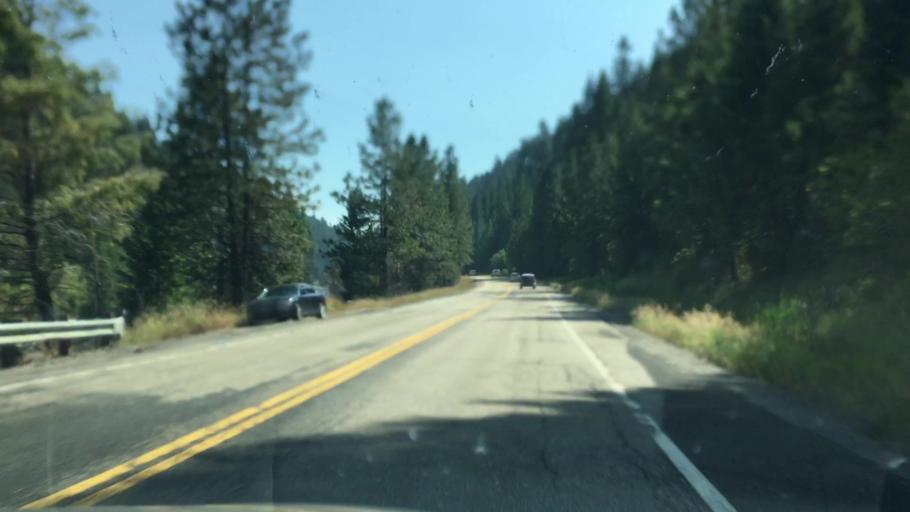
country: US
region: Idaho
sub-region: Valley County
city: Cascade
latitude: 44.2383
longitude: -116.1030
